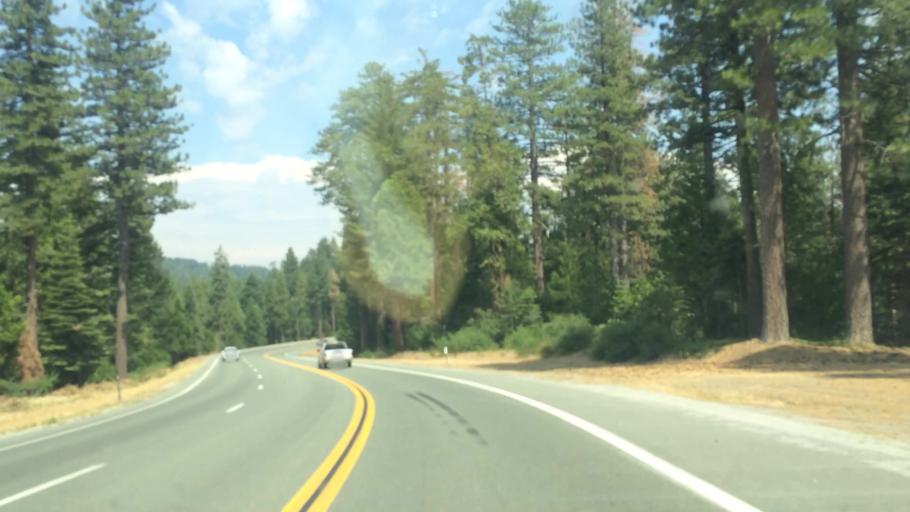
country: US
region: California
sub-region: Amador County
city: Pioneer
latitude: 38.5306
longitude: -120.4192
